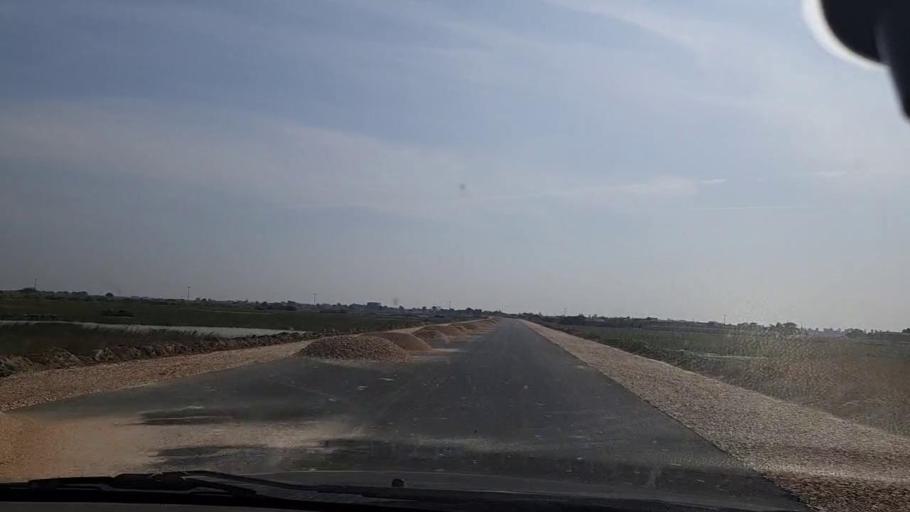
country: PK
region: Sindh
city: Mirpur Batoro
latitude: 24.7476
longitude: 68.2717
